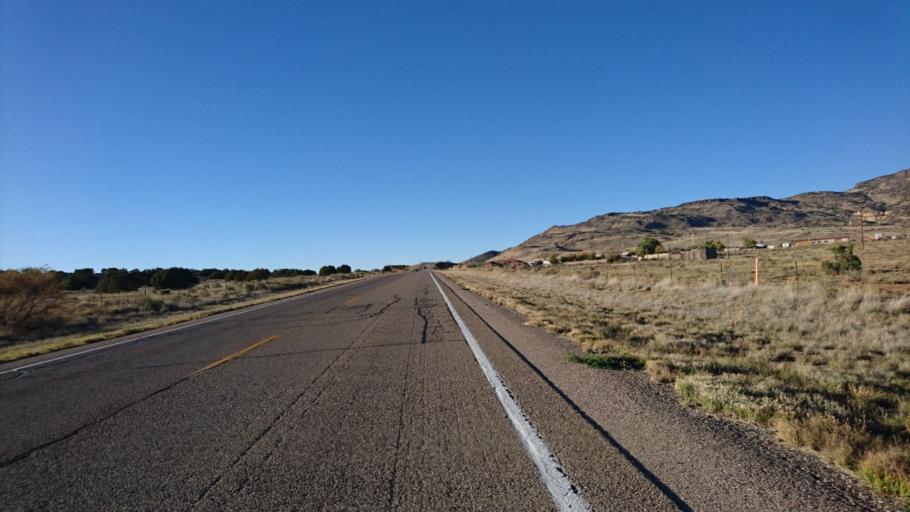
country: US
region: New Mexico
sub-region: Cibola County
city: Grants
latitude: 35.1007
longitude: -107.7760
